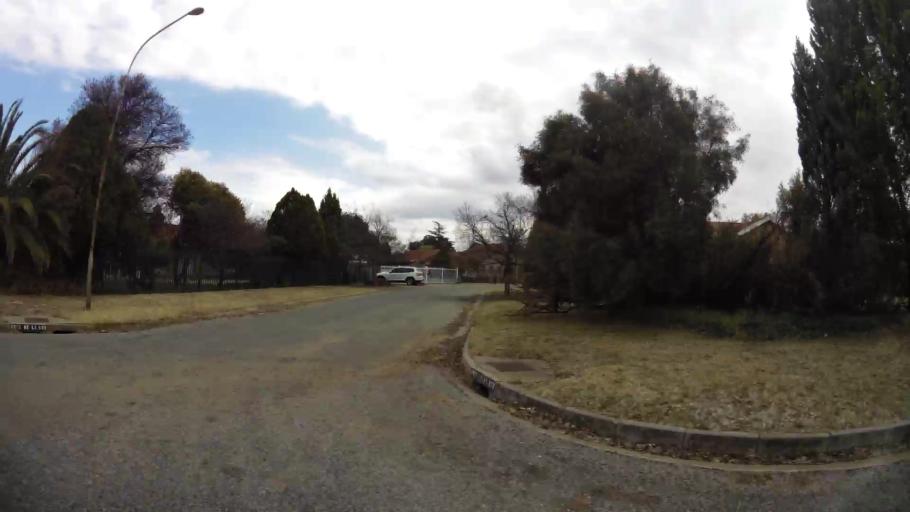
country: ZA
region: Orange Free State
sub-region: Fezile Dabi District Municipality
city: Kroonstad
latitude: -27.6378
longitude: 27.2406
